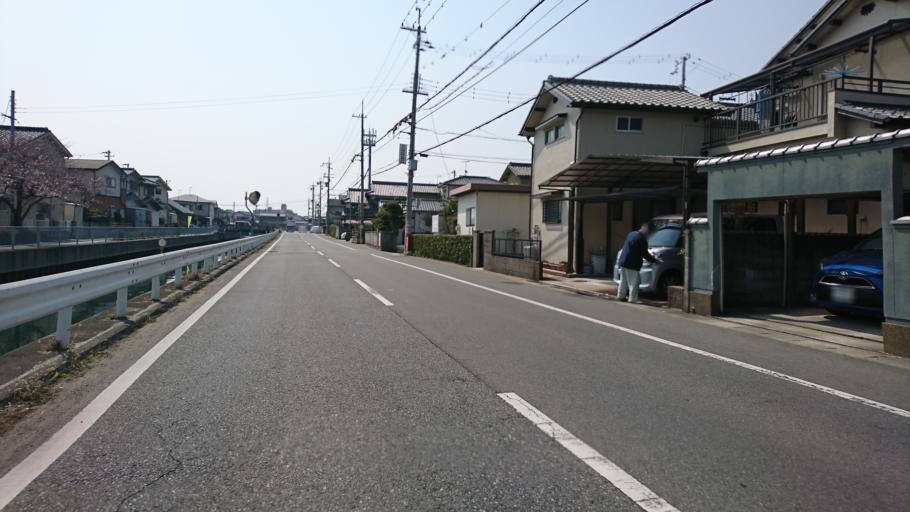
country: JP
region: Hyogo
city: Shirahamacho-usazakiminami
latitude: 34.7846
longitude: 134.7512
